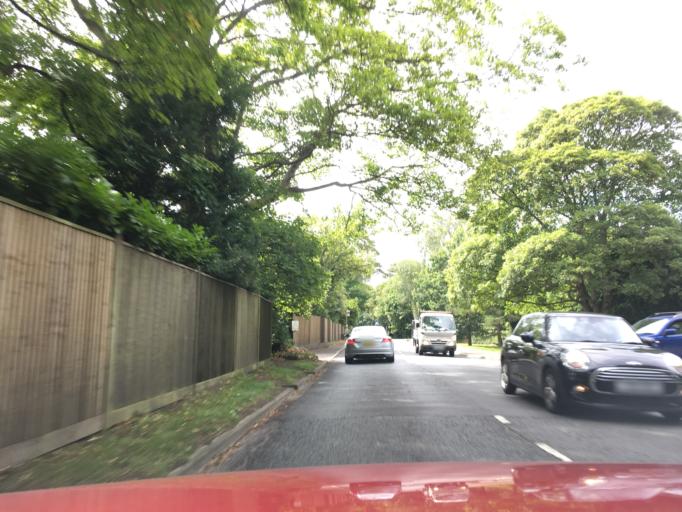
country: GB
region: England
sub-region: Kent
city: Royal Tunbridge Wells
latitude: 51.1305
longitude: 0.2230
